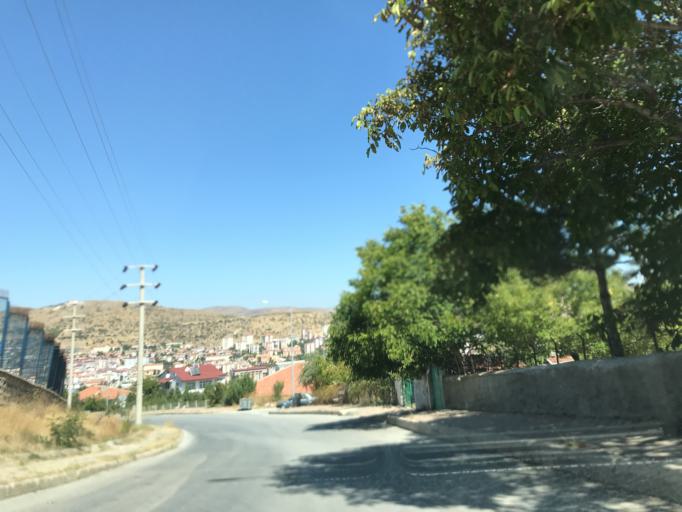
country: TR
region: Yozgat
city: Yozgat
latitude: 39.8150
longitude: 34.8227
